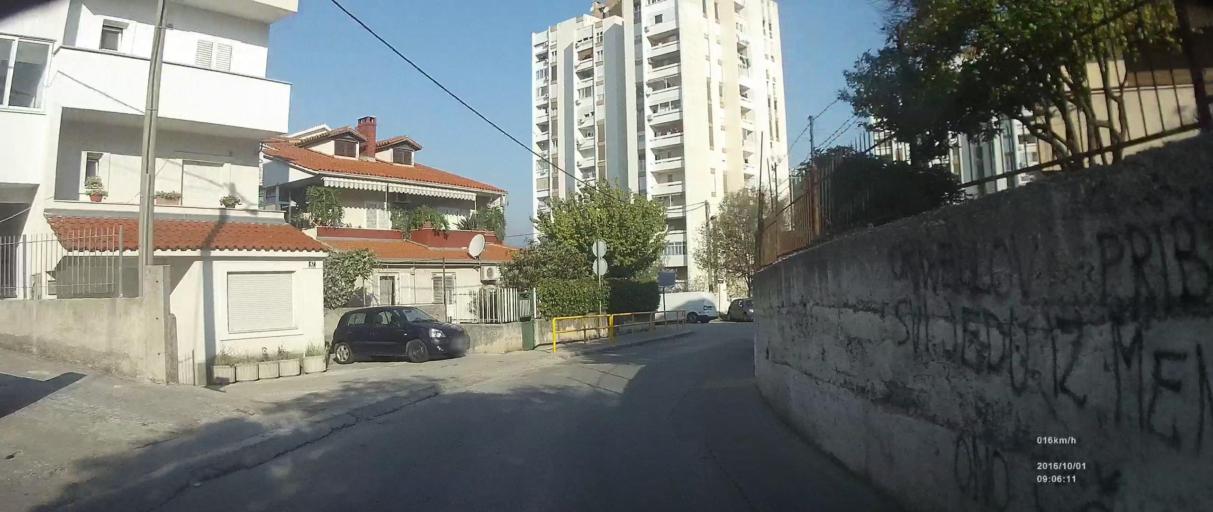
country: HR
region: Splitsko-Dalmatinska
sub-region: Grad Split
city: Split
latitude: 43.5181
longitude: 16.4514
